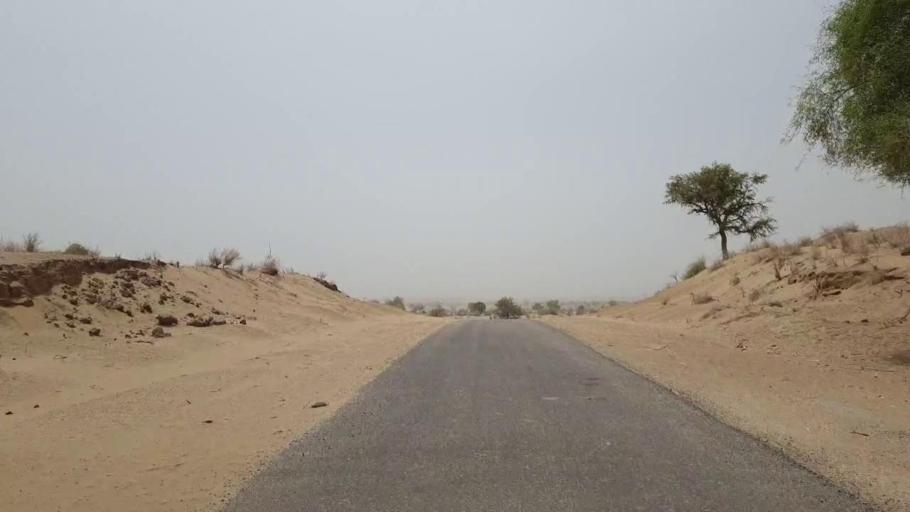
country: PK
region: Sindh
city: Islamkot
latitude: 24.7893
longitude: 70.5112
